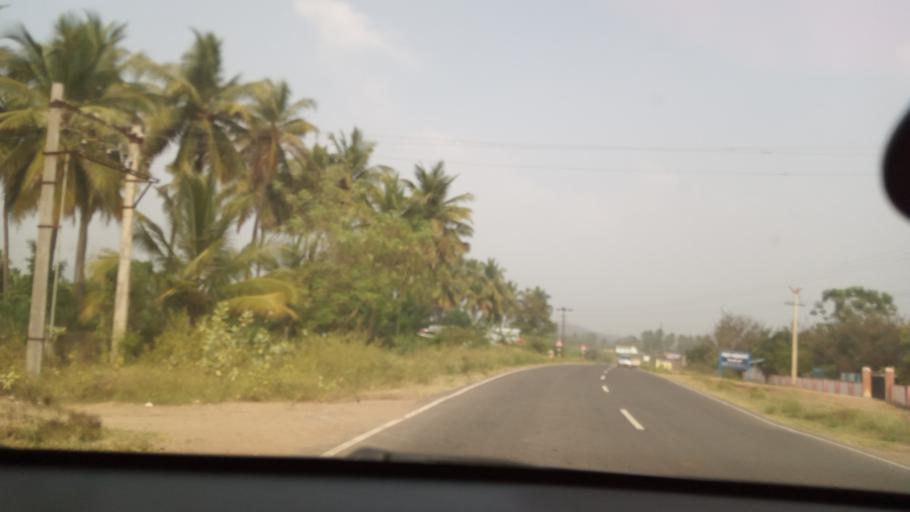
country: IN
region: Tamil Nadu
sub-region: Erode
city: Sathyamangalam
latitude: 11.5302
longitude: 77.1398
